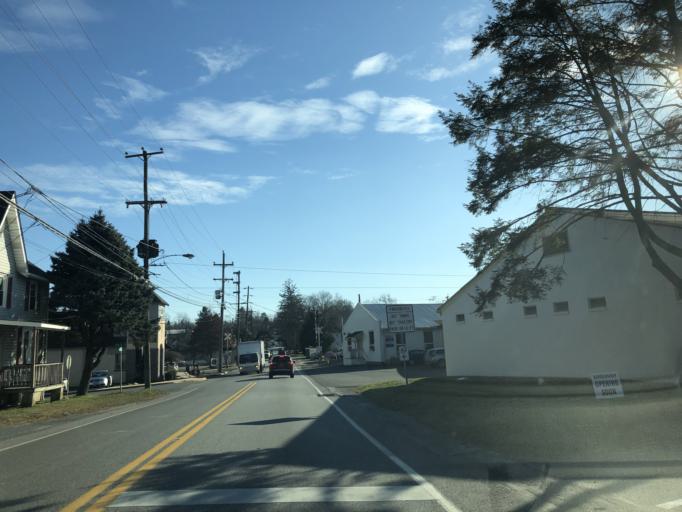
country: US
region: Pennsylvania
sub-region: Chester County
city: Toughkenamon
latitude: 39.8314
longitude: -75.7575
